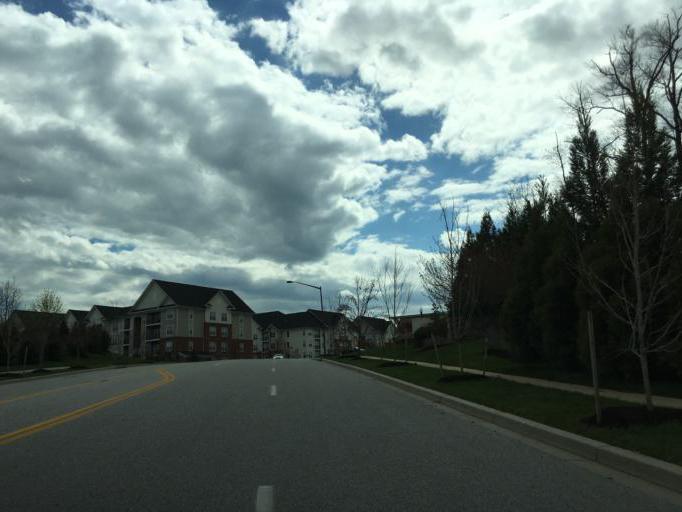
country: US
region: Maryland
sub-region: Anne Arundel County
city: Jessup
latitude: 39.1558
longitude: -76.7409
